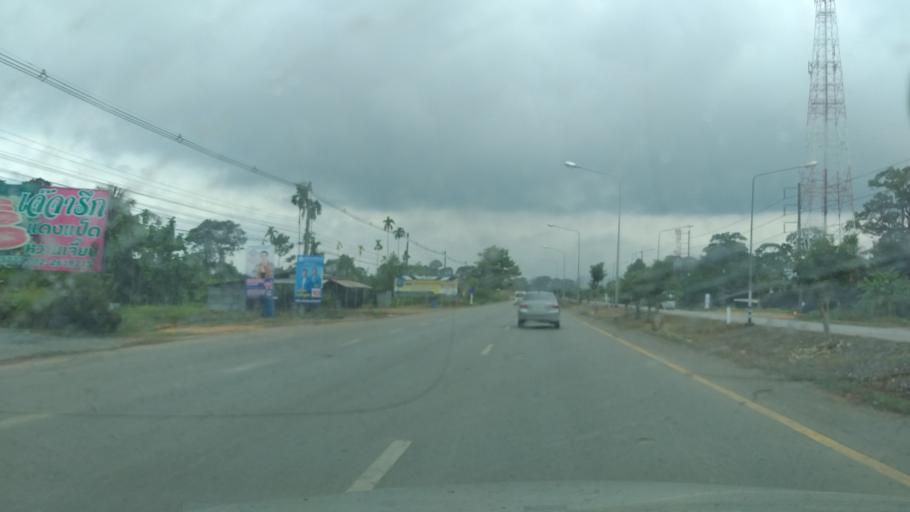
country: TH
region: Chanthaburi
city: Khlung
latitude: 12.4546
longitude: 102.2775
